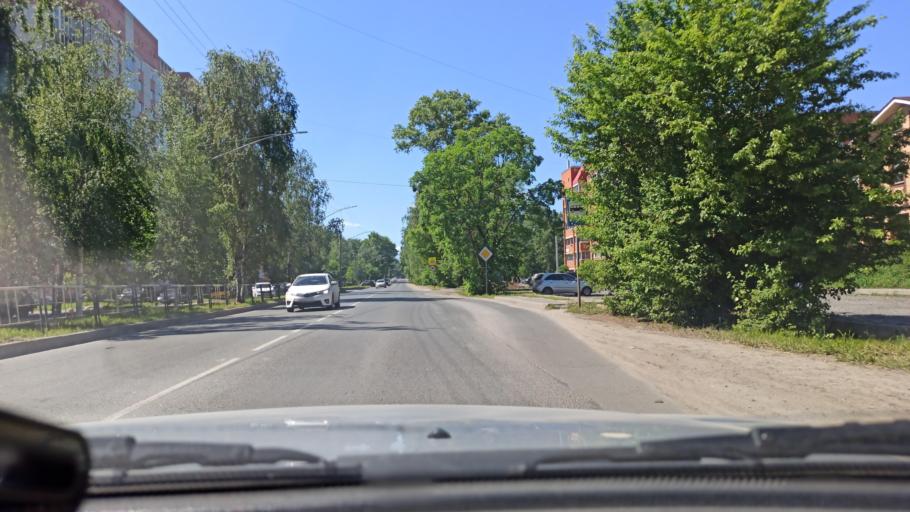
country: RU
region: Vologda
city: Vologda
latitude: 59.2154
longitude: 39.8459
